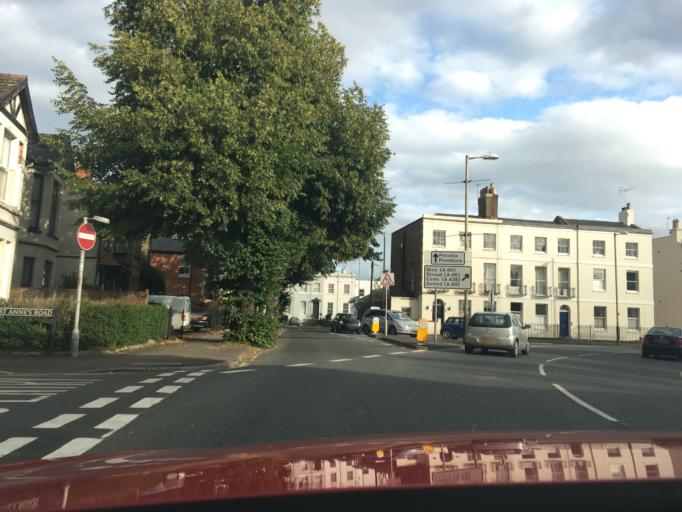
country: GB
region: England
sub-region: Gloucestershire
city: Cheltenham
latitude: 51.8986
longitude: -2.0683
